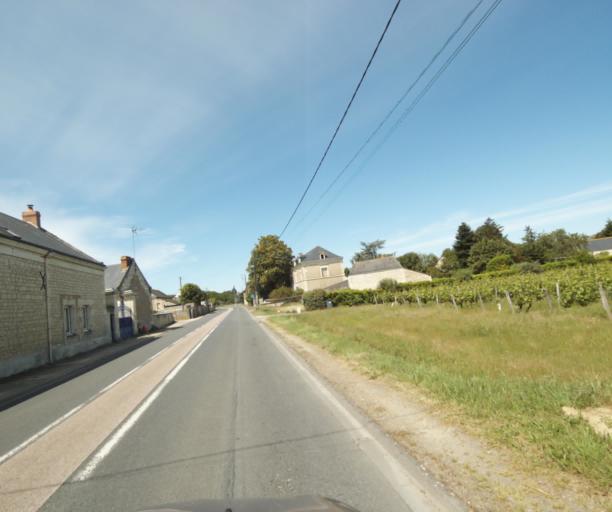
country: FR
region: Centre
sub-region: Departement d'Indre-et-Loire
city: Ligre
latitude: 47.1354
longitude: 0.3087
